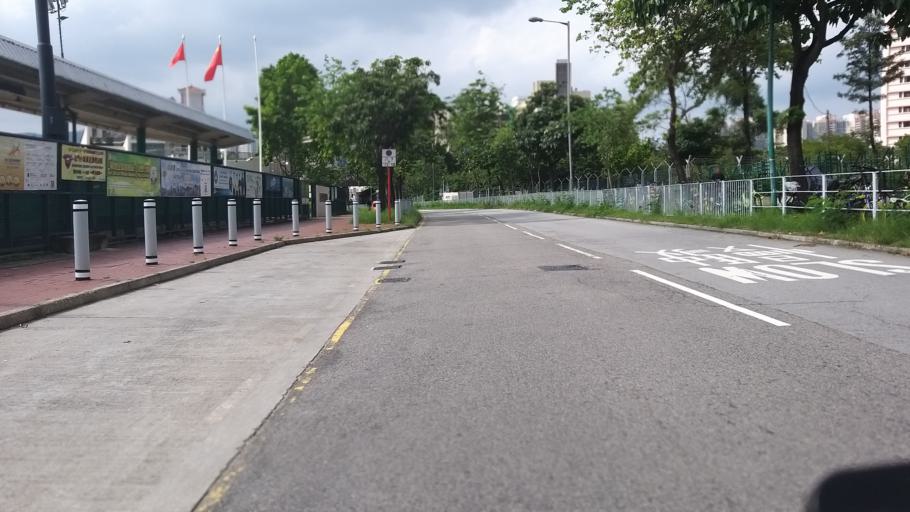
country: HK
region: Tuen Mun
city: Tuen Mun
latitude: 22.4041
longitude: 113.9747
